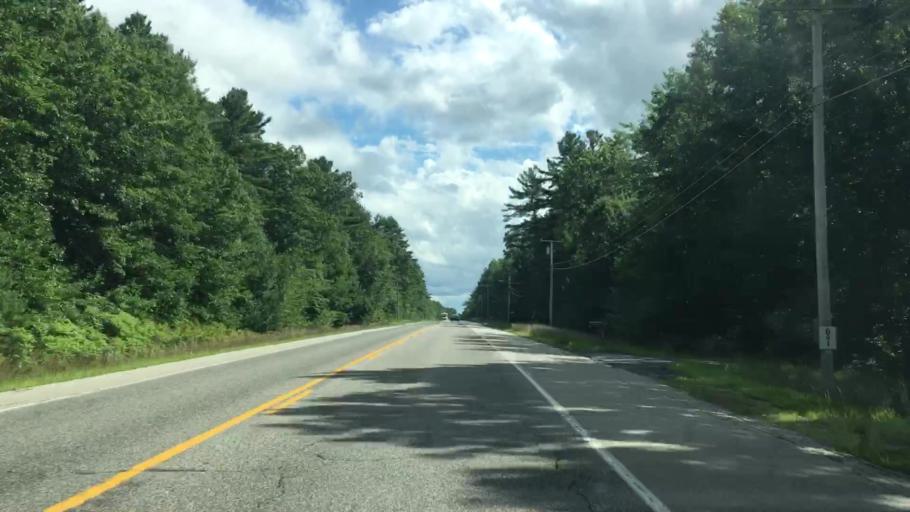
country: US
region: Maine
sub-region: York County
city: South Sanford
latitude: 43.3689
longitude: -70.7332
